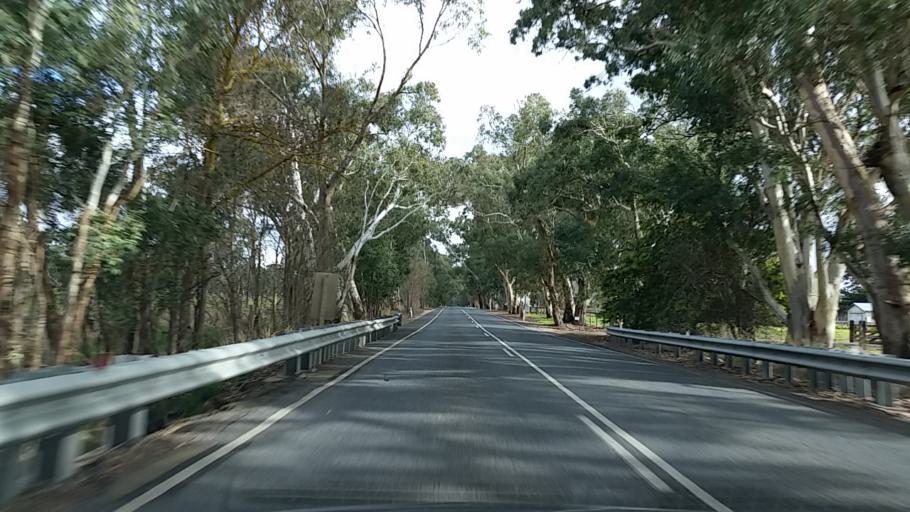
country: AU
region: South Australia
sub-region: Mount Barker
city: Meadows
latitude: -35.1946
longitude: 138.7270
